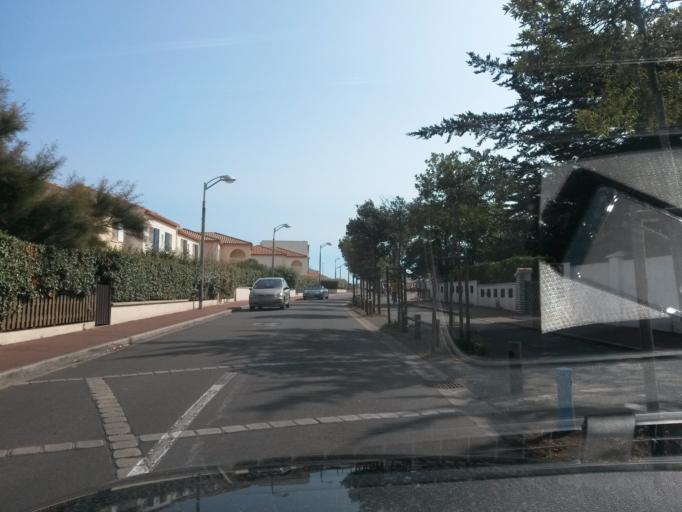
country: FR
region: Pays de la Loire
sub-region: Departement de la Vendee
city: Bretignolles-sur-Mer
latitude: 46.6254
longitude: -1.8737
